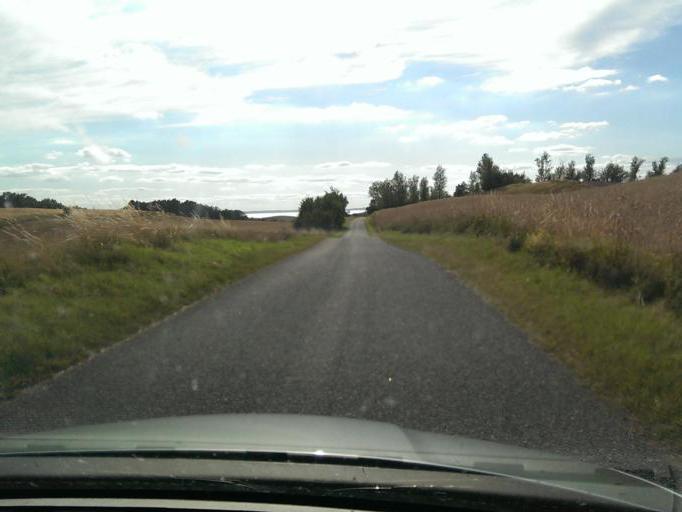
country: DK
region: Central Jutland
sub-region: Syddjurs Kommune
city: Ebeltoft
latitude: 56.1173
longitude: 10.5172
